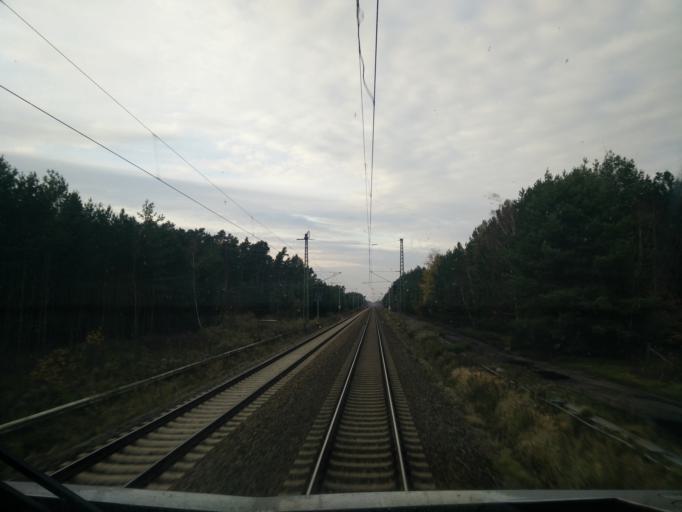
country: DE
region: Brandenburg
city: Halbe
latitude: 52.1187
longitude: 13.6910
